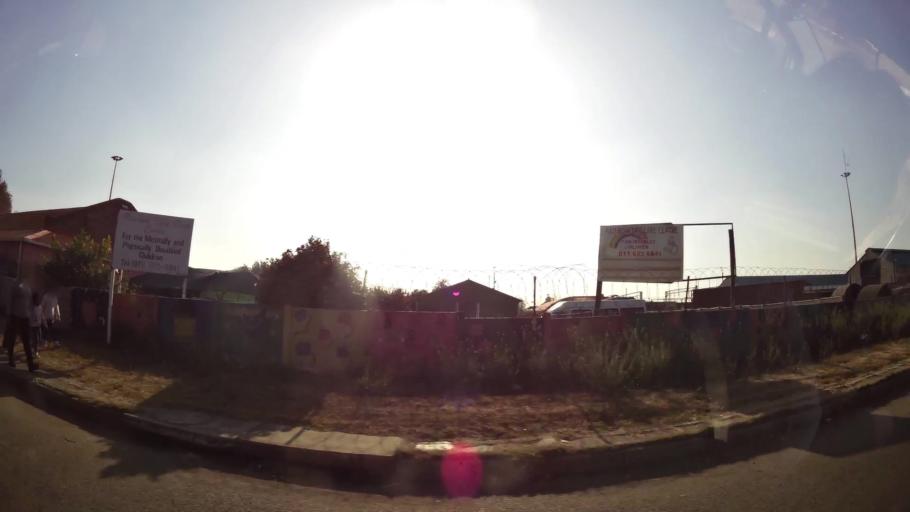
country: ZA
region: Gauteng
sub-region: West Rand District Municipality
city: Randfontein
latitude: -26.1586
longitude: 27.7166
